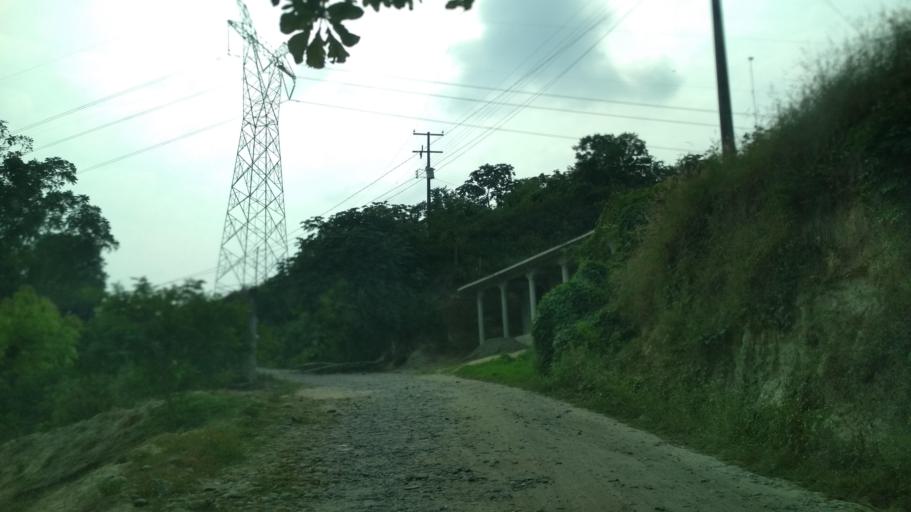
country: MM
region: Kayah
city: Loikaw
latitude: 20.2195
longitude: 97.2849
